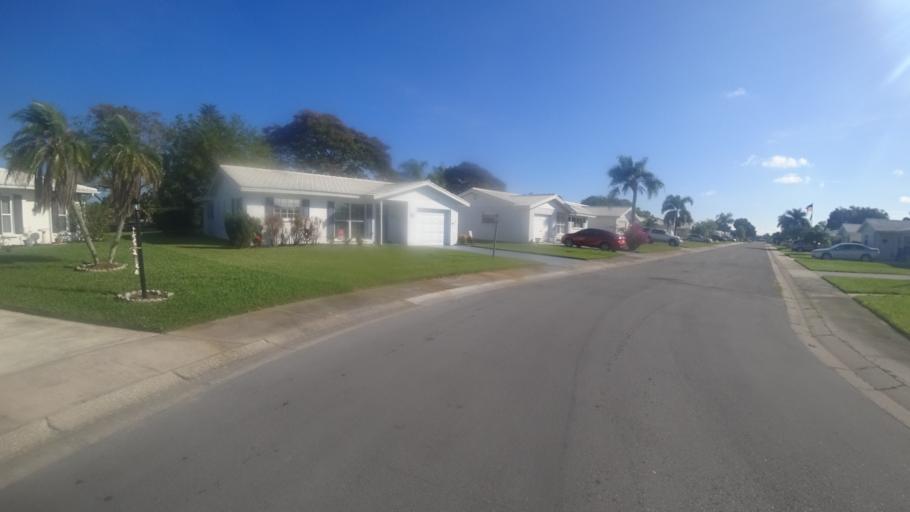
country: US
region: Florida
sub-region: Manatee County
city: Ellenton
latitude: 27.4970
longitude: -82.5139
